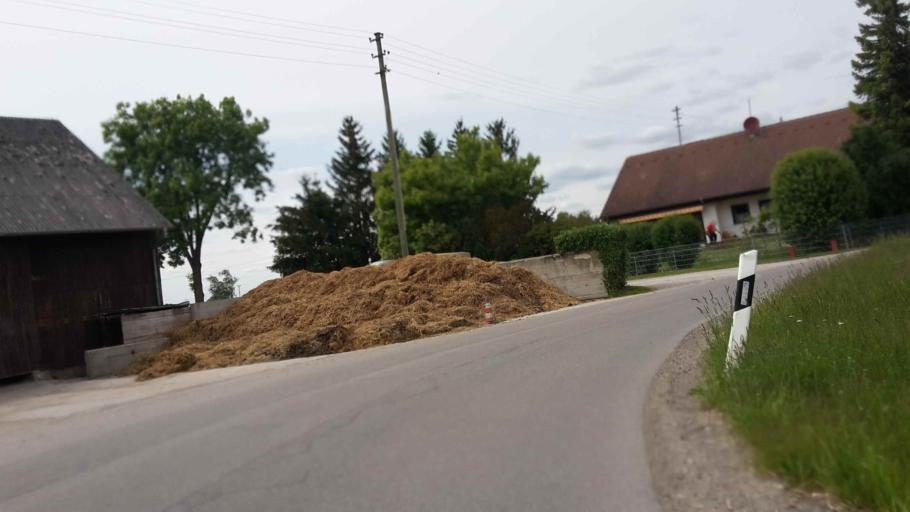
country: DE
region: Bavaria
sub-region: Upper Bavaria
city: Dachau
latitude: 48.2202
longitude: 11.4233
